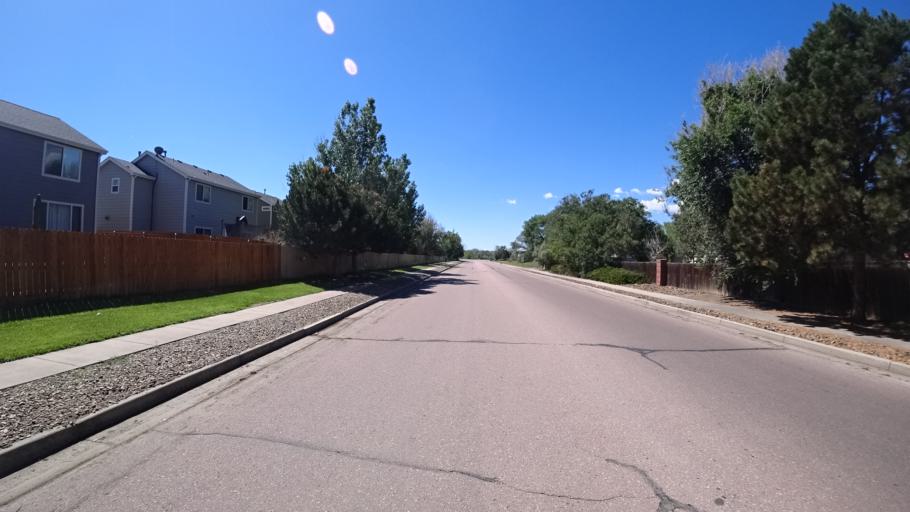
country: US
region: Colorado
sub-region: El Paso County
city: Security-Widefield
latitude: 38.7646
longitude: -104.6550
